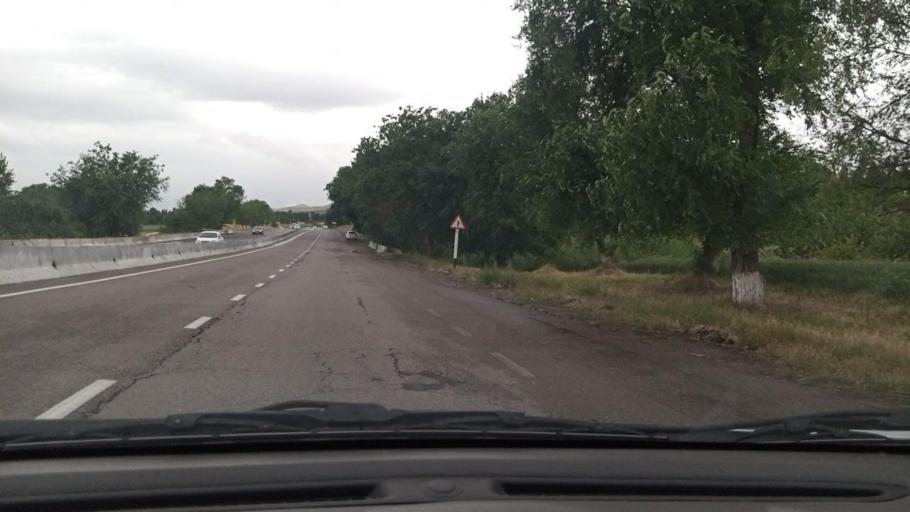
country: UZ
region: Toshkent
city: Angren
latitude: 40.9653
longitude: 69.9572
